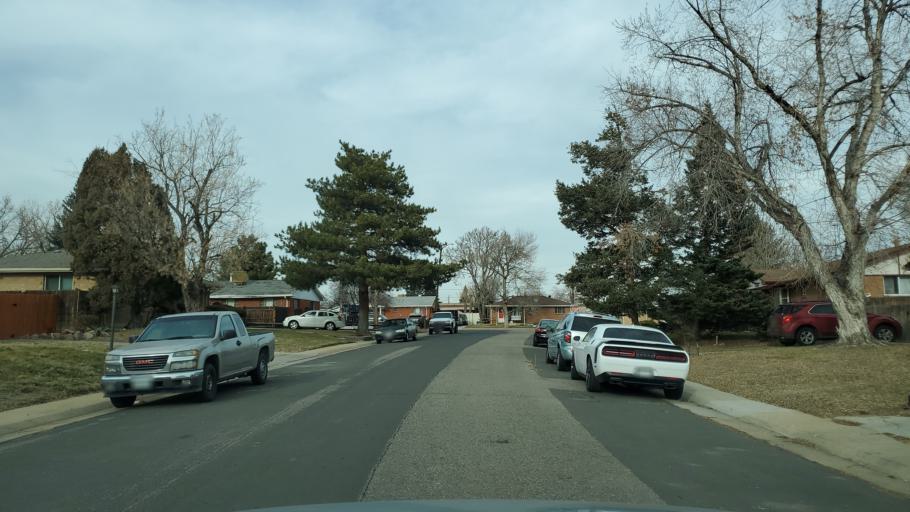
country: US
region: Colorado
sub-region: Adams County
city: Westminster
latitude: 39.8334
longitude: -105.0206
